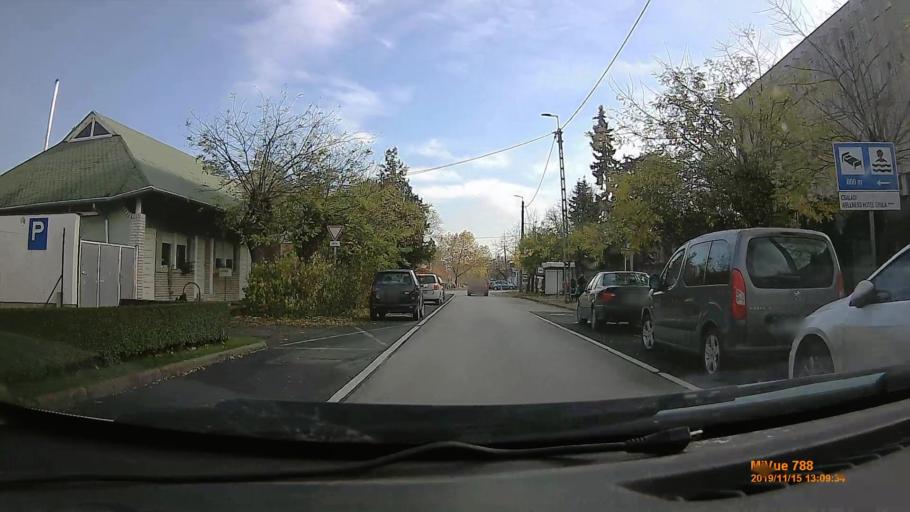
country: HU
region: Bekes
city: Gyula
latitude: 46.6415
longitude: 21.2781
